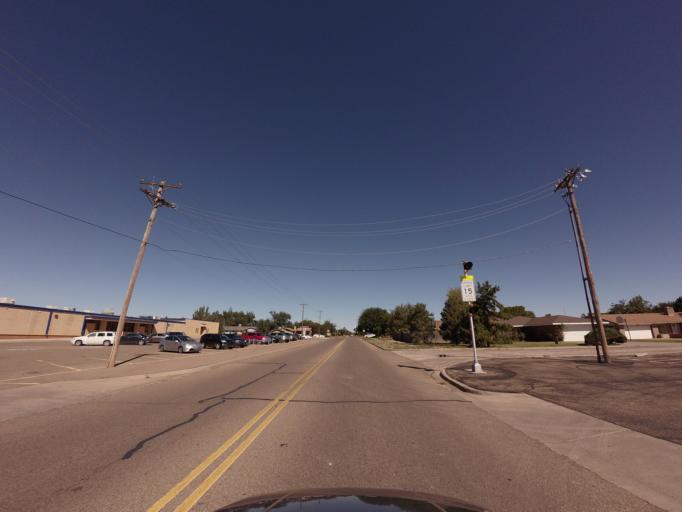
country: US
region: New Mexico
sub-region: Curry County
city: Clovis
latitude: 34.4141
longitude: -103.1877
